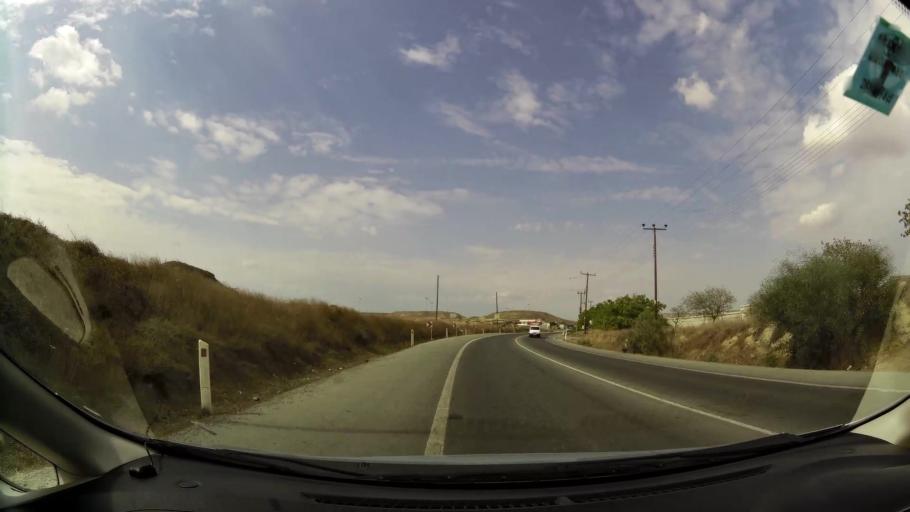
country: CY
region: Lefkosia
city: Dali
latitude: 35.0523
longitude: 33.3795
